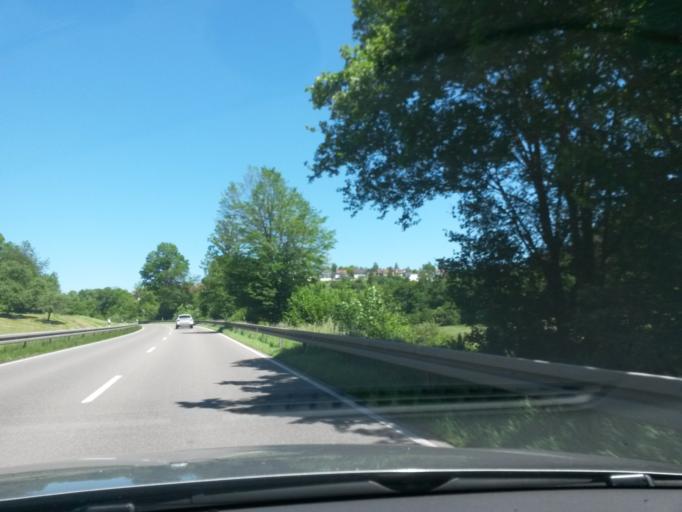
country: DE
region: Baden-Wuerttemberg
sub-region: Regierungsbezirk Stuttgart
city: Aidlingen
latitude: 48.7046
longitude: 8.9150
